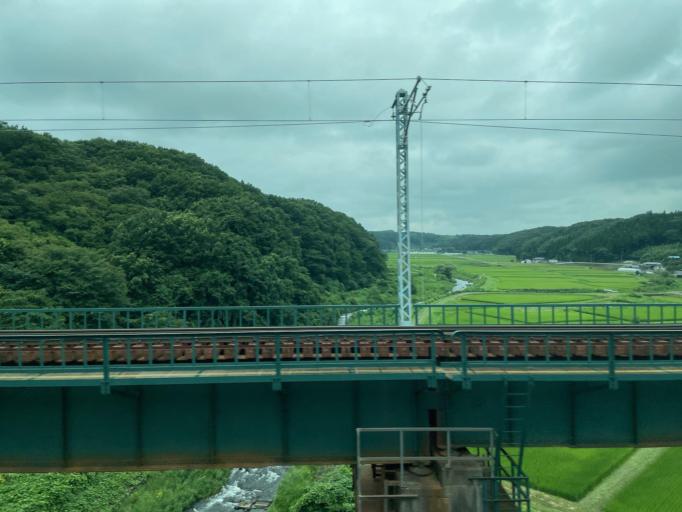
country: JP
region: Tochigi
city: Kuroiso
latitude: 37.0761
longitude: 140.1684
